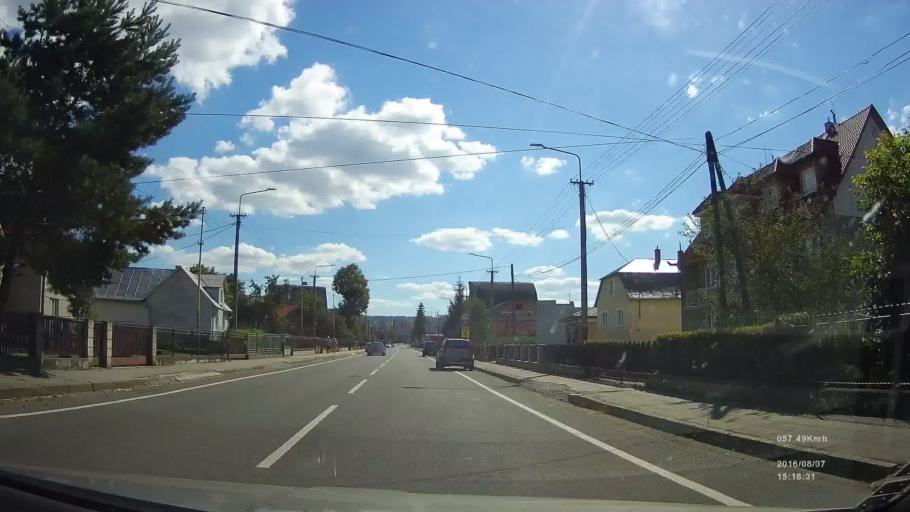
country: SK
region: Presovsky
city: Stropkov
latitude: 49.2103
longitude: 21.6541
